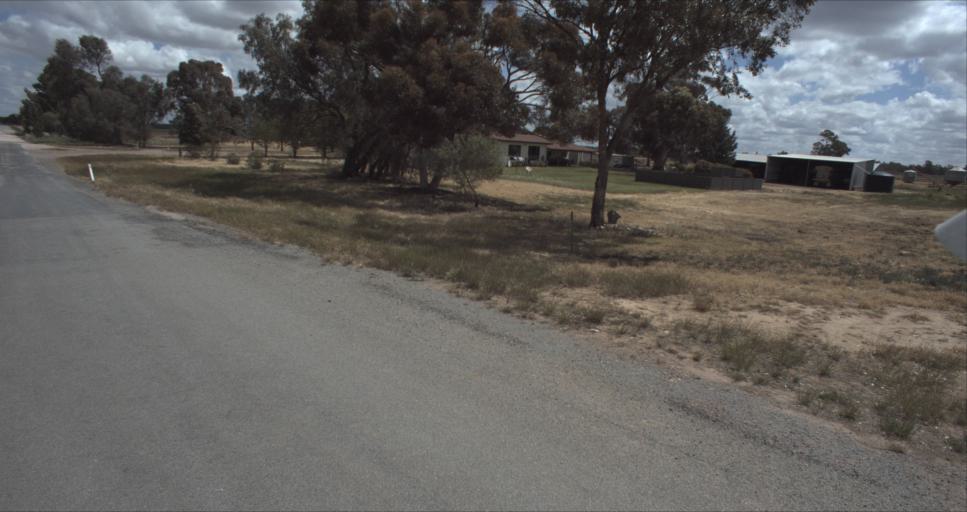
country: AU
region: New South Wales
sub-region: Leeton
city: Leeton
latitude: -34.5879
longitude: 146.3615
